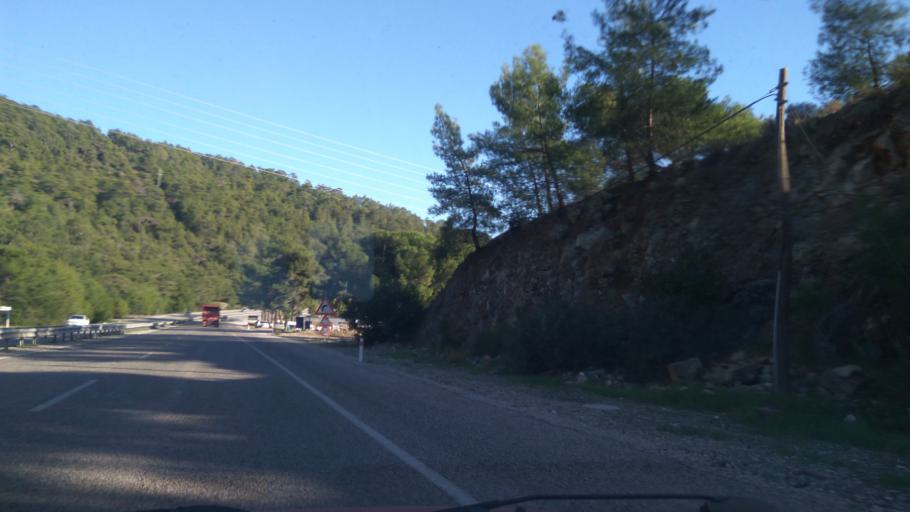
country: TR
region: Antalya
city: Kemer
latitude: 36.5822
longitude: 30.5501
